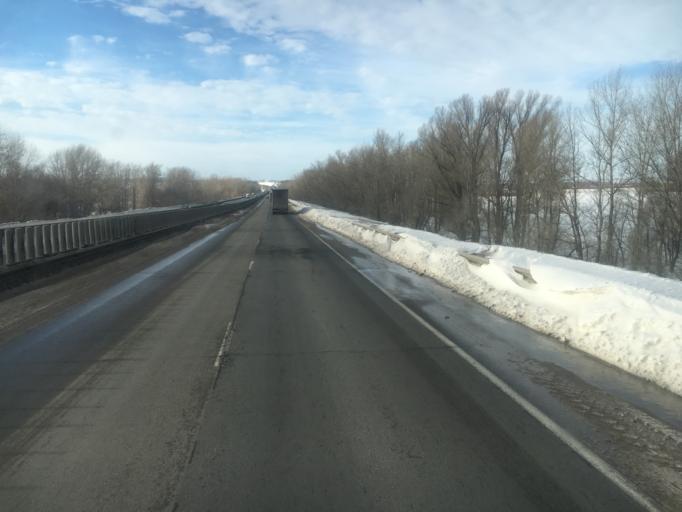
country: RU
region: Samara
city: Mirnyy
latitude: 53.4347
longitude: 50.2917
